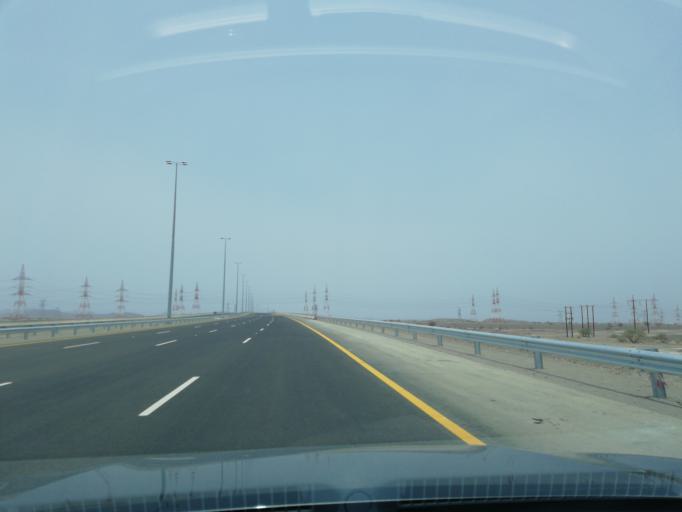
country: OM
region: Al Batinah
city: Al Liwa'
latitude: 24.4173
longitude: 56.5343
